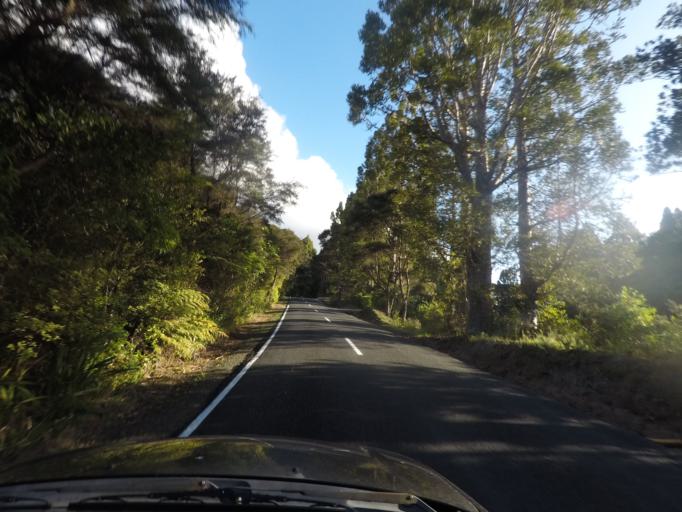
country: NZ
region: Auckland
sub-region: Auckland
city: Titirangi
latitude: -36.9304
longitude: 174.6185
